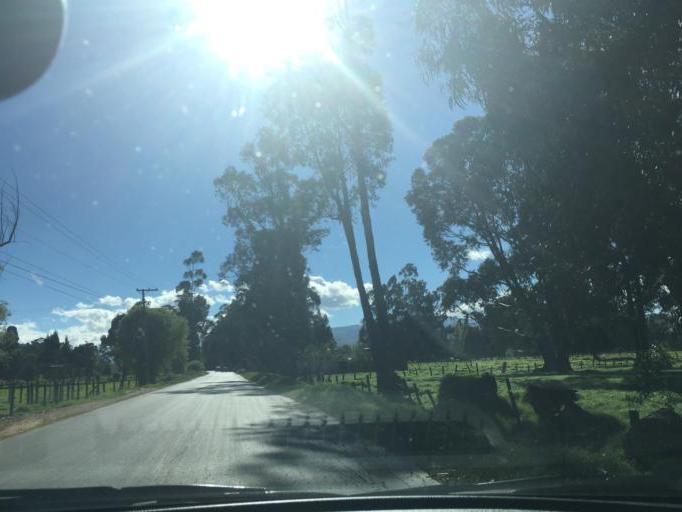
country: CO
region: Boyaca
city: Firavitoba
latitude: 5.6602
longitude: -72.9758
